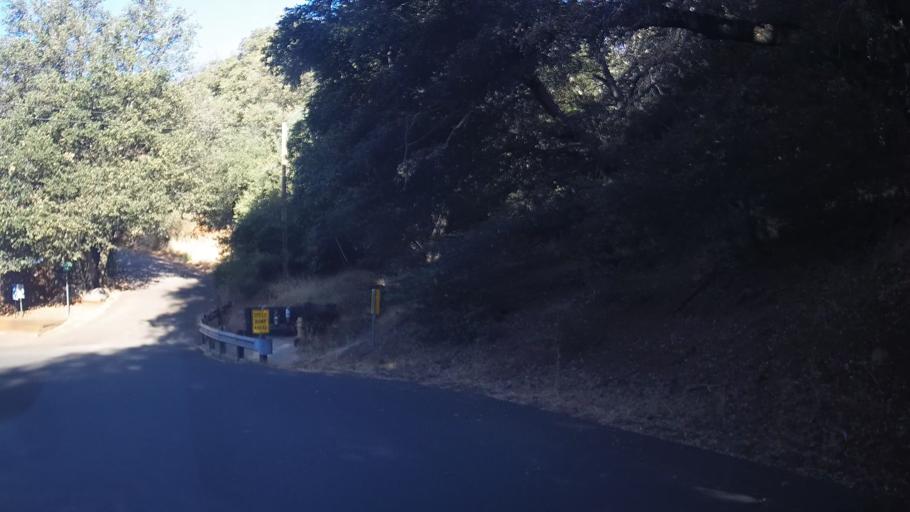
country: US
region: California
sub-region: San Diego County
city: Julian
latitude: 33.0436
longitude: -116.6210
